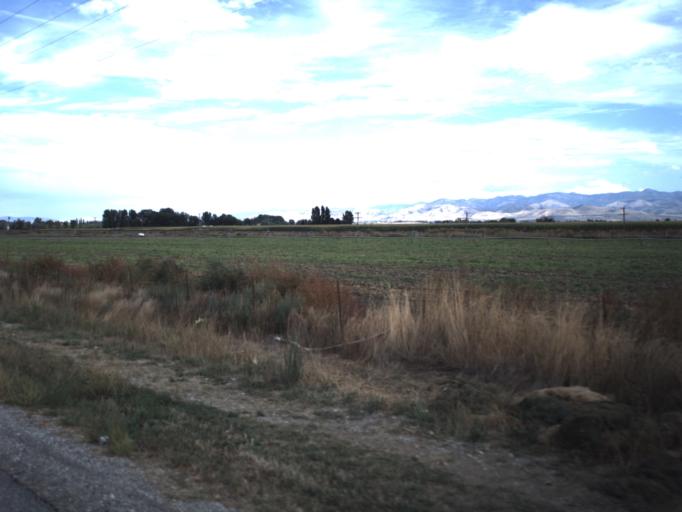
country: US
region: Utah
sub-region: Cache County
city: Lewiston
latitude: 41.9768
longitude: -111.9542
